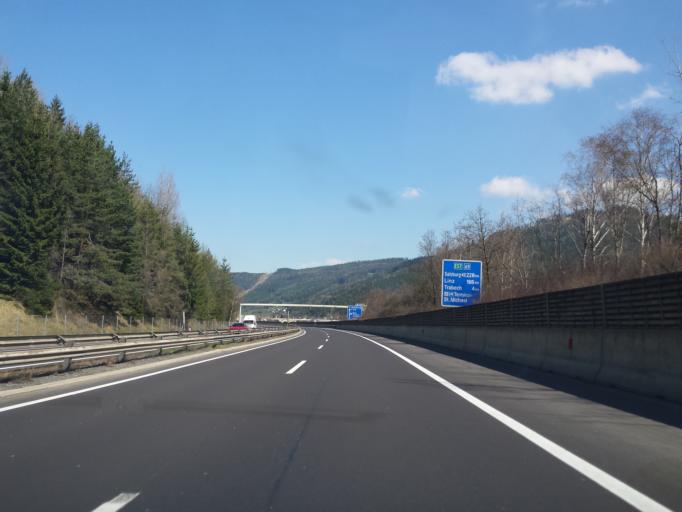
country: AT
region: Styria
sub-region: Politischer Bezirk Leoben
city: Sankt Michael in Obersteiermark
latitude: 47.3445
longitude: 15.0074
